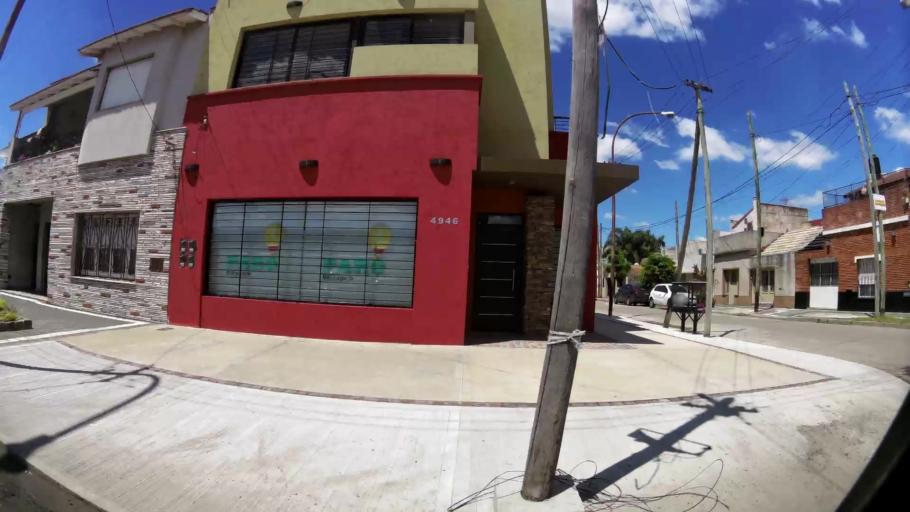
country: AR
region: Buenos Aires
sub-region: Partido de Lanus
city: Lanus
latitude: -34.7297
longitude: -58.4064
